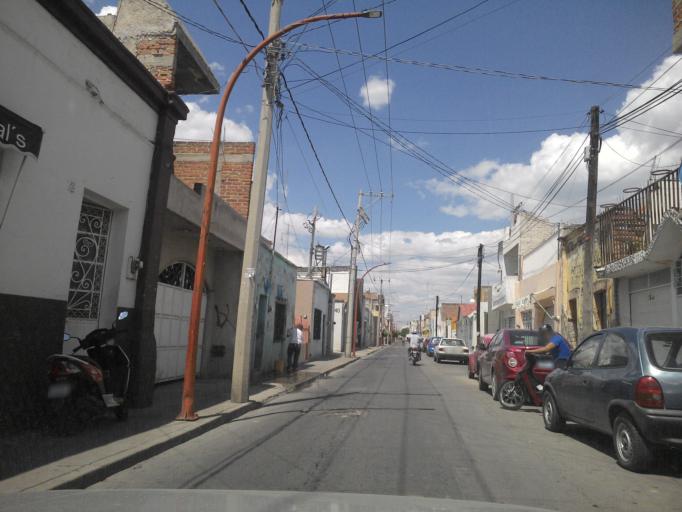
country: MX
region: Guanajuato
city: San Francisco del Rincon
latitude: 21.0195
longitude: -101.8616
